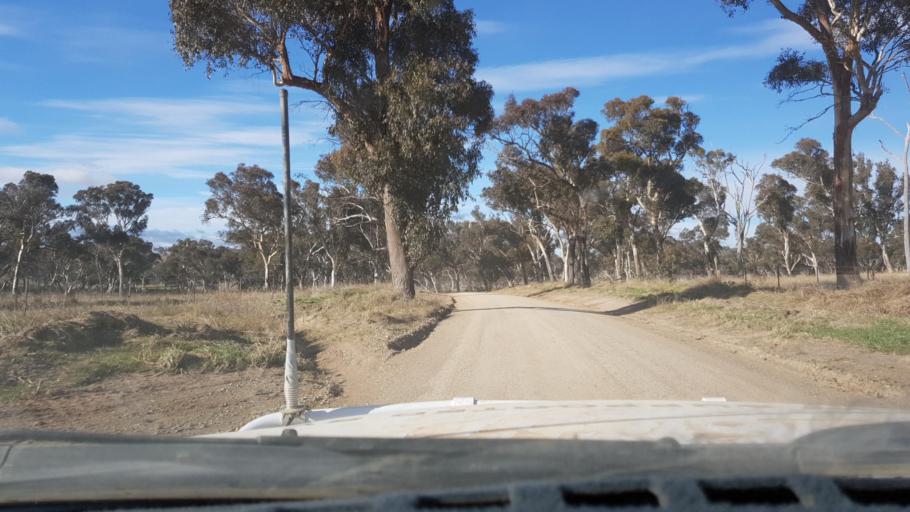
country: AU
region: New South Wales
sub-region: Armidale Dumaresq
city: Enmore
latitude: -30.7187
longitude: 151.5895
